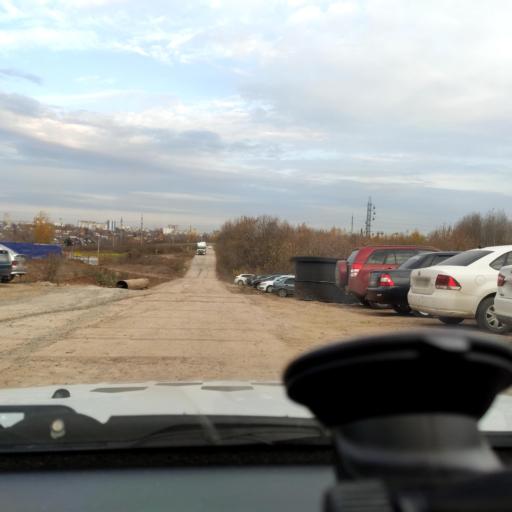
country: RU
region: Perm
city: Perm
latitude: 58.0118
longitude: 56.3312
